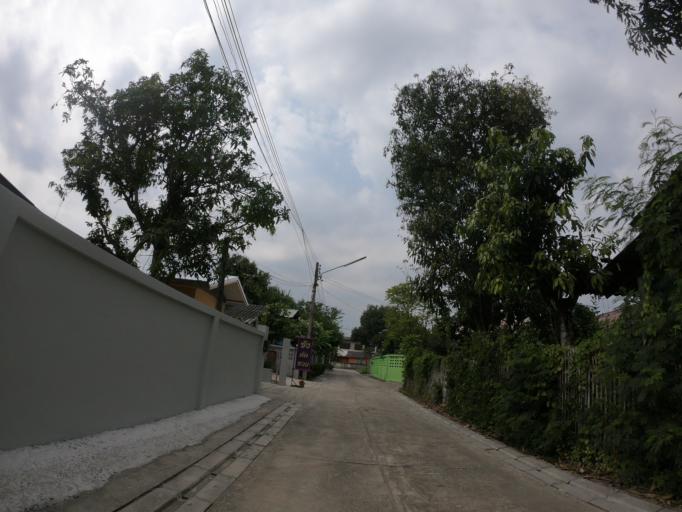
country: TH
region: Chiang Mai
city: Chiang Mai
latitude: 18.7586
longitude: 98.9842
